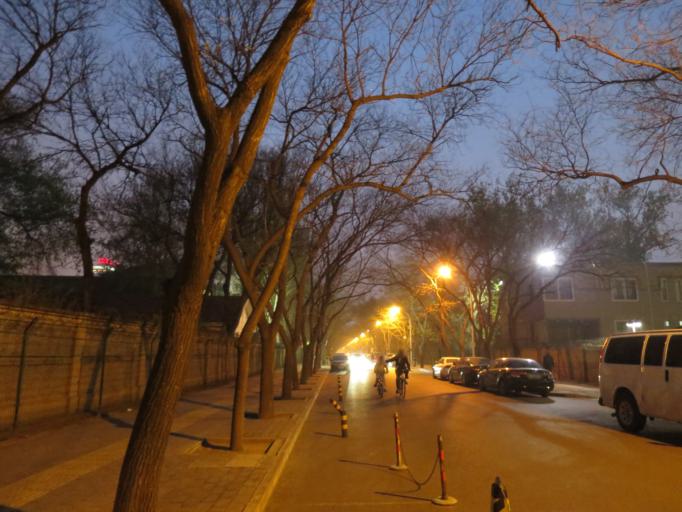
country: CN
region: Beijing
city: Chaowai
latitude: 39.9105
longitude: 116.4424
